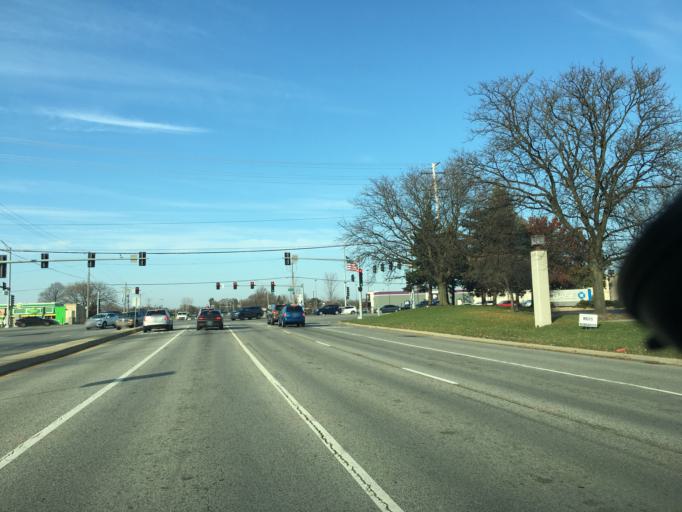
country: US
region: Illinois
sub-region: DuPage County
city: Woodridge
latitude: 41.7503
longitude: -88.0126
